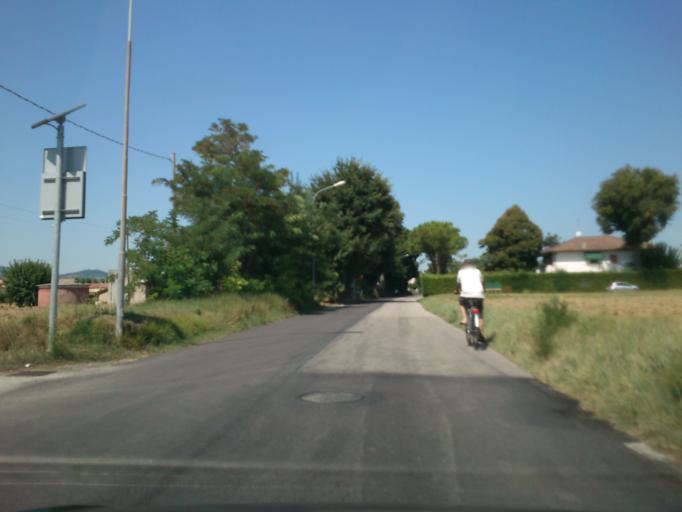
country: IT
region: The Marches
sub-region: Provincia di Pesaro e Urbino
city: Lucrezia
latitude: 43.7717
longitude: 12.9448
